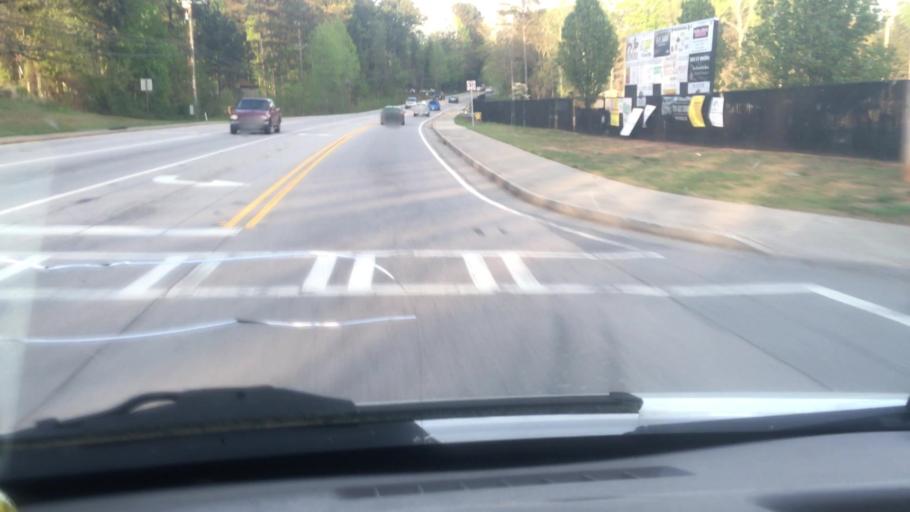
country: US
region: Georgia
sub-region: Paulding County
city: Hiram
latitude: 33.9414
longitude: -84.7463
